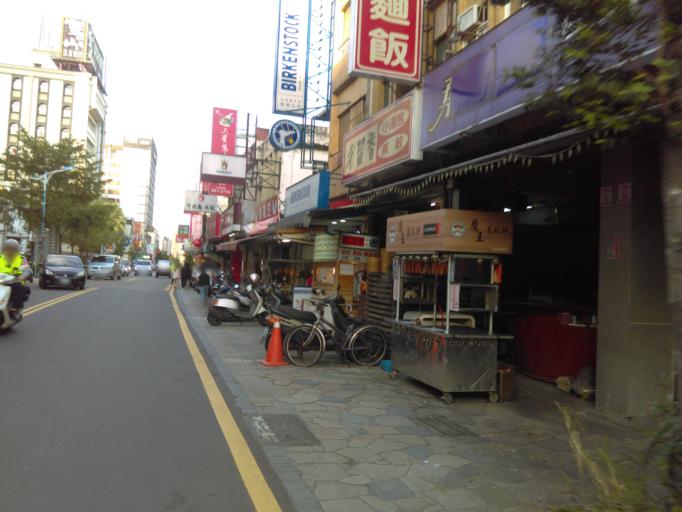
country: TW
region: Taiwan
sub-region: Yilan
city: Yilan
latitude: 24.8266
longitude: 121.7735
